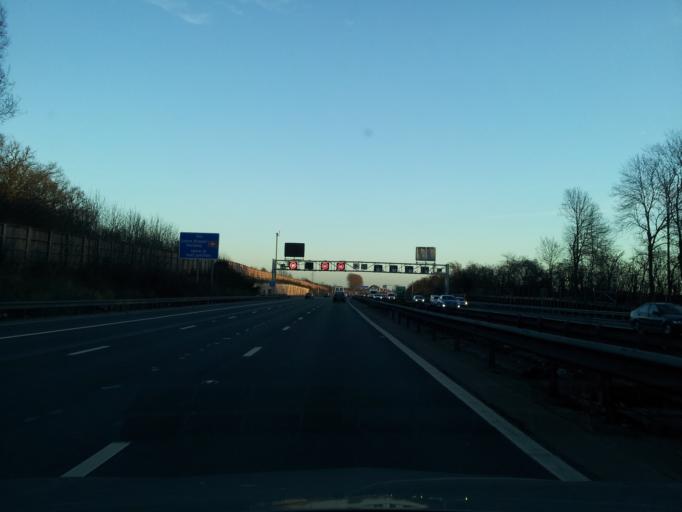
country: GB
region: England
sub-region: Central Bedfordshire
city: Caddington
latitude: 51.8761
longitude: -0.4469
